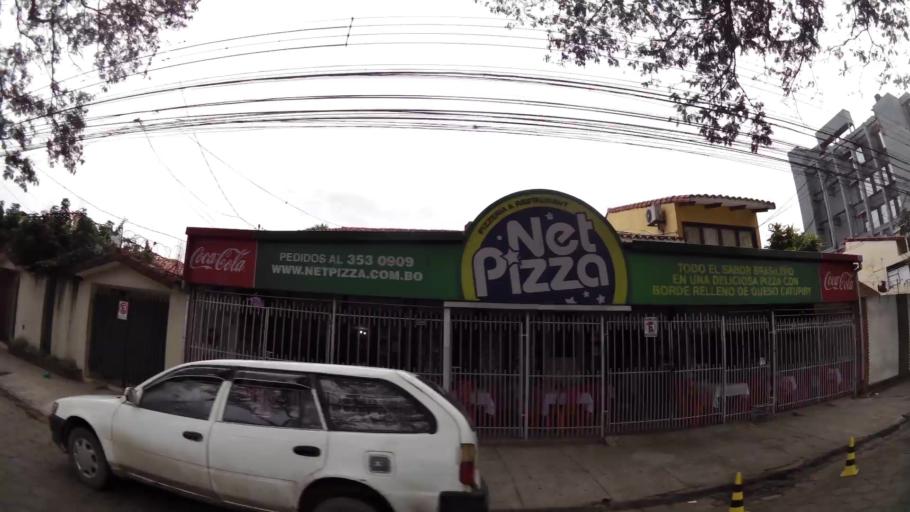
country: BO
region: Santa Cruz
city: Santa Cruz de la Sierra
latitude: -17.7977
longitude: -63.1834
